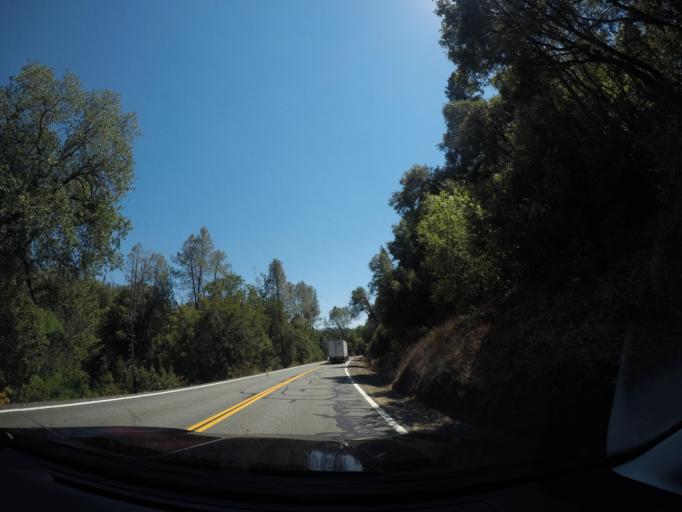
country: US
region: California
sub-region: Shasta County
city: Bella Vista
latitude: 40.7207
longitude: -122.0819
